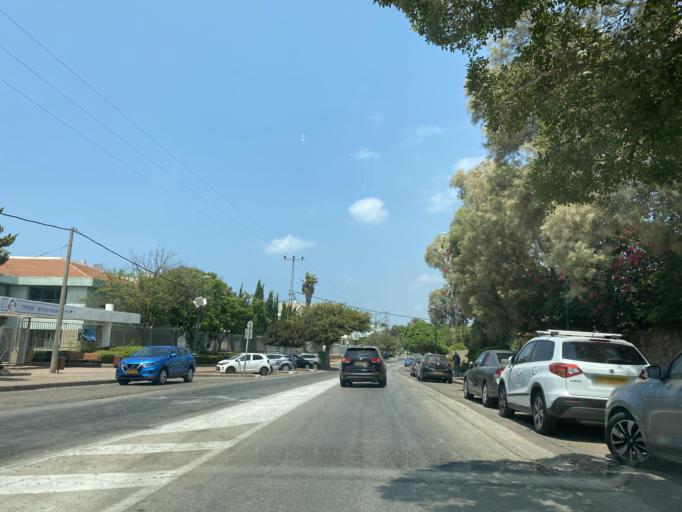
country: IL
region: Tel Aviv
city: Herzliya Pituah
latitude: 32.1683
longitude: 34.8034
